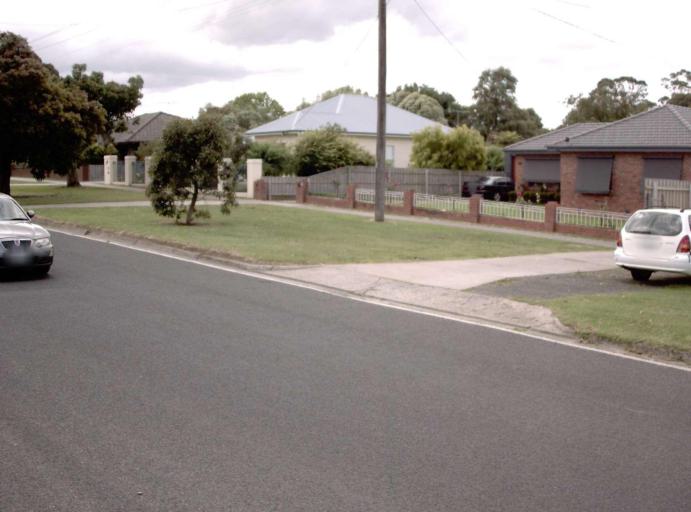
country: AU
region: Victoria
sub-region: Baw Baw
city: Warragul
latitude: -38.1273
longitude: 145.8468
